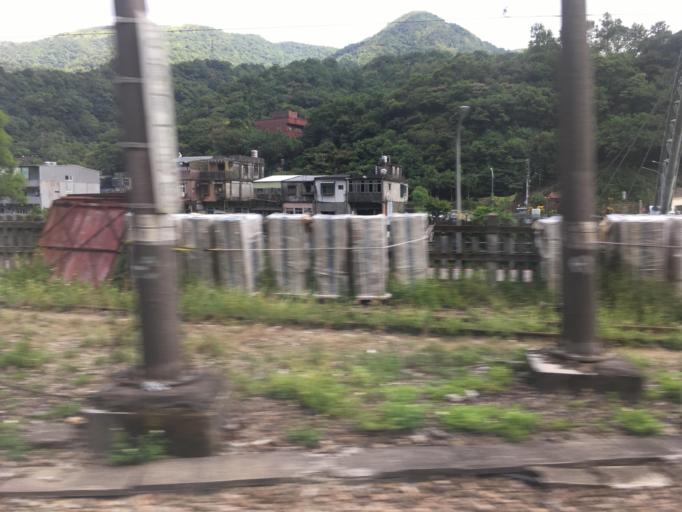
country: TW
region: Taiwan
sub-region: Keelung
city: Keelung
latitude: 25.0893
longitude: 121.8288
